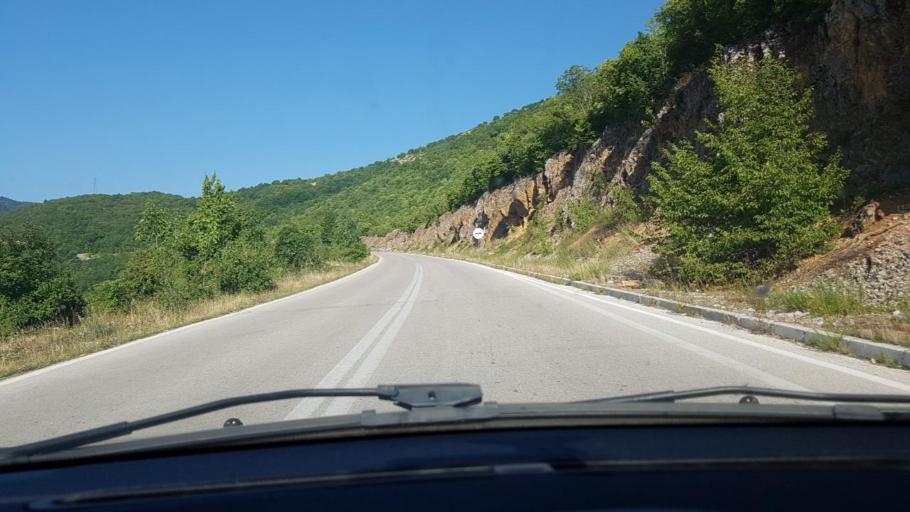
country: BA
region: Federation of Bosnia and Herzegovina
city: Rumboci
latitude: 43.8206
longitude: 17.4548
